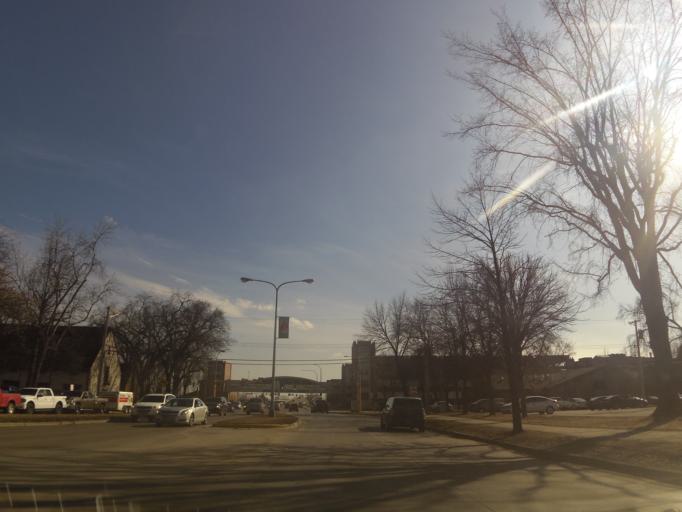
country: US
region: North Dakota
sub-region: Grand Forks County
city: Grand Forks
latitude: 47.9234
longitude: -97.0666
